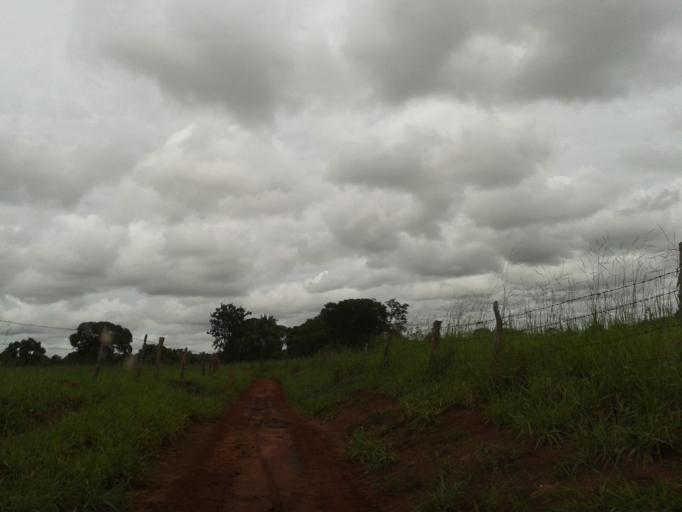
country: BR
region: Minas Gerais
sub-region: Capinopolis
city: Capinopolis
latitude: -18.7844
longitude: -49.7855
